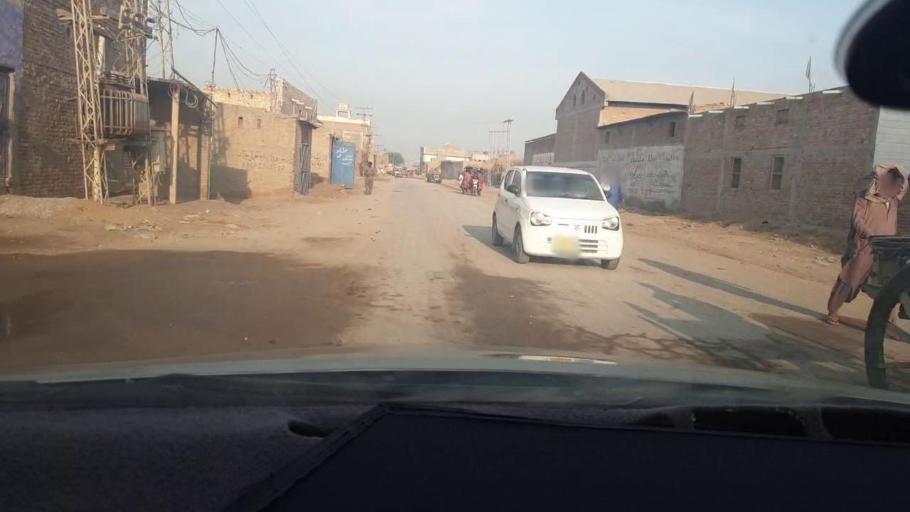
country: PK
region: Sindh
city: Jacobabad
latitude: 28.2836
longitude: 68.4270
